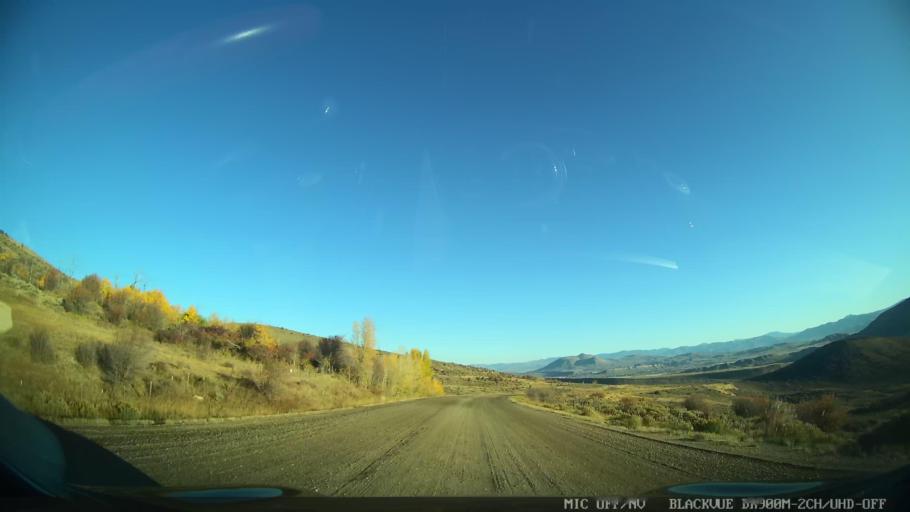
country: US
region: Colorado
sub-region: Grand County
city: Kremmling
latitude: 40.0019
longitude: -106.4059
